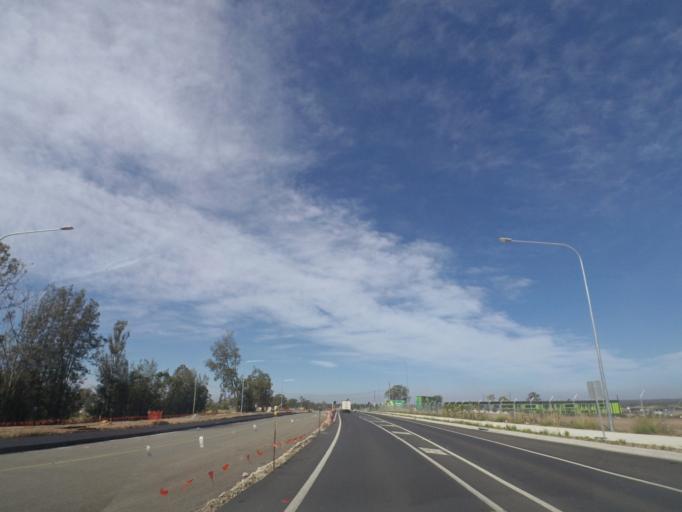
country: AU
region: New South Wales
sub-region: Campbelltown Municipality
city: Denham Court
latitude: -33.9753
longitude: 150.8548
